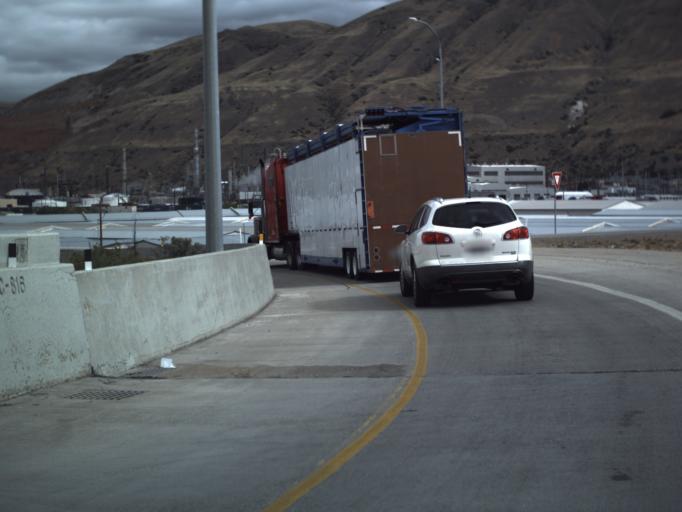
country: US
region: Utah
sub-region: Salt Lake County
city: Salt Lake City
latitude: 40.7826
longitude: -111.9105
